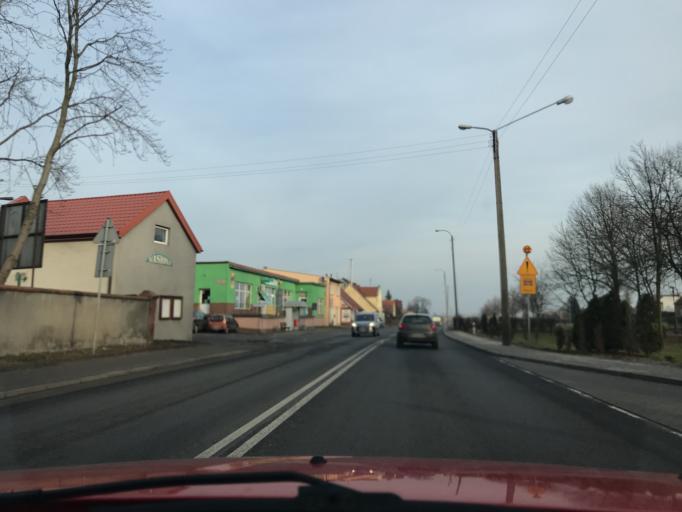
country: PL
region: Greater Poland Voivodeship
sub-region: Powiat jarocinski
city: Witaszyce
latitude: 51.9421
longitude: 17.5638
